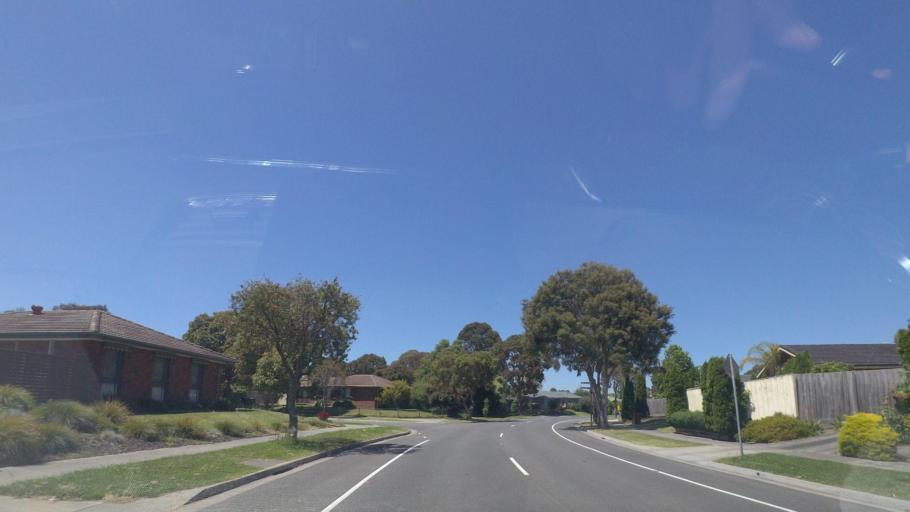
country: AU
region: Victoria
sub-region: Knox
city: Knoxfield
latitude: -37.8942
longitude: 145.2683
